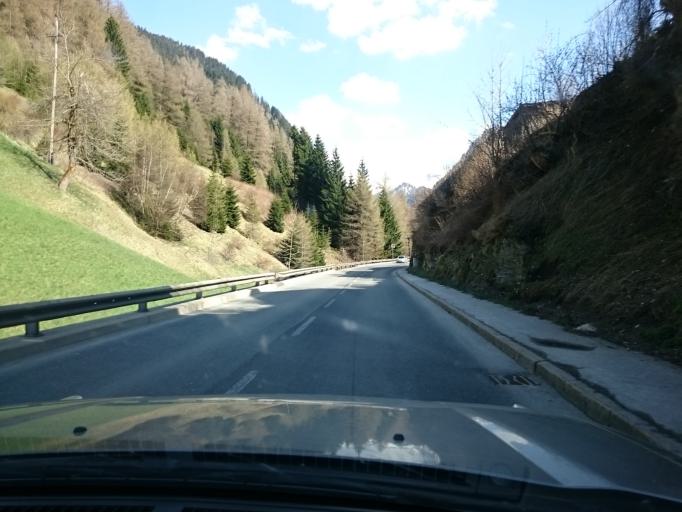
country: AT
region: Tyrol
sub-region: Politischer Bezirk Innsbruck Land
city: Gries am Brenner
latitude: 47.0349
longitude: 11.4831
